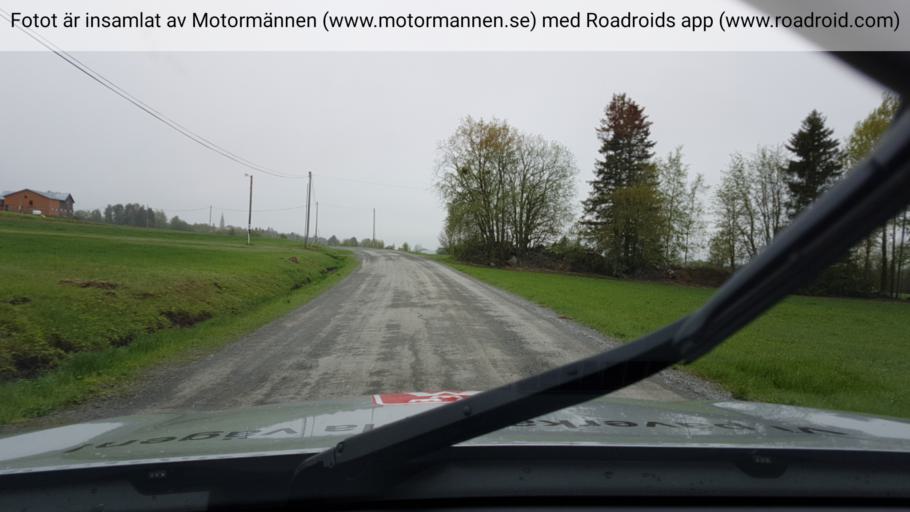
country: SE
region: Jaemtland
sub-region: Bergs Kommun
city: Hoverberg
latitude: 63.0085
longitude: 14.3855
